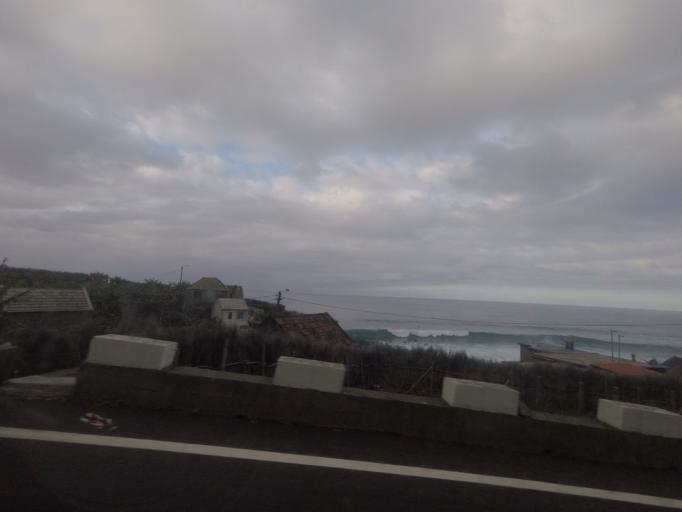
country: PT
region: Madeira
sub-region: Porto Moniz
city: Porto Moniz
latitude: 32.8418
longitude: -17.1416
